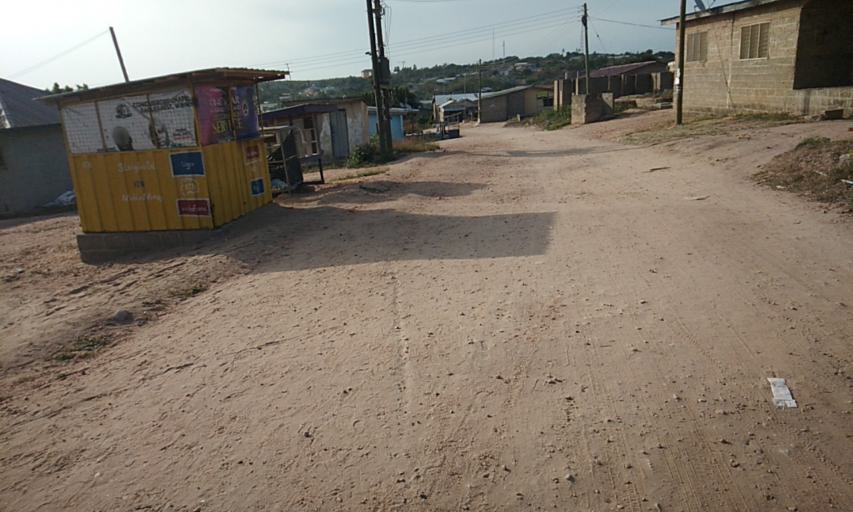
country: GH
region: Central
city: Winneba
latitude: 5.3583
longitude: -0.6148
